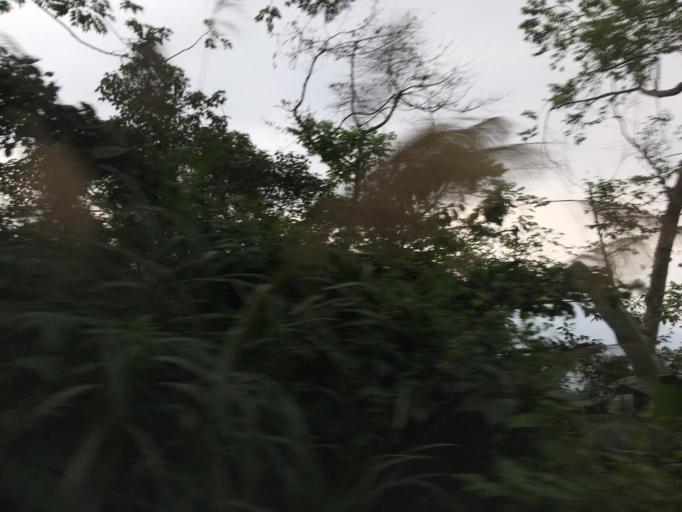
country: TW
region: Taiwan
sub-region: Chiayi
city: Jiayi Shi
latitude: 23.5360
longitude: 120.6301
